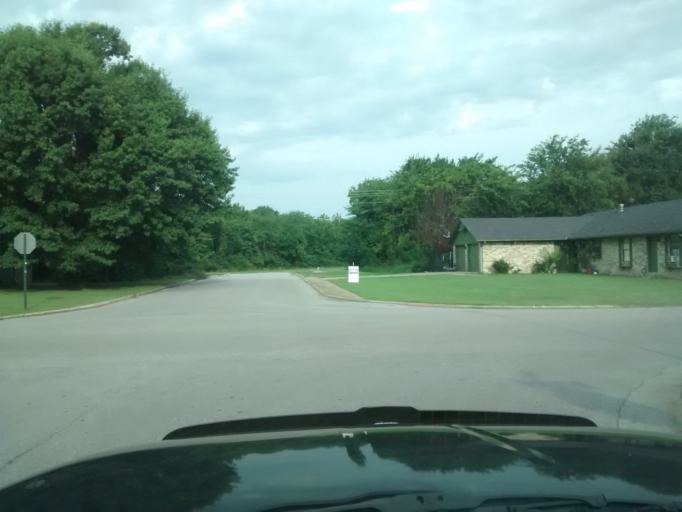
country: US
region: Arkansas
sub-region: Washington County
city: Fayetteville
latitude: 36.0751
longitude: -94.2059
